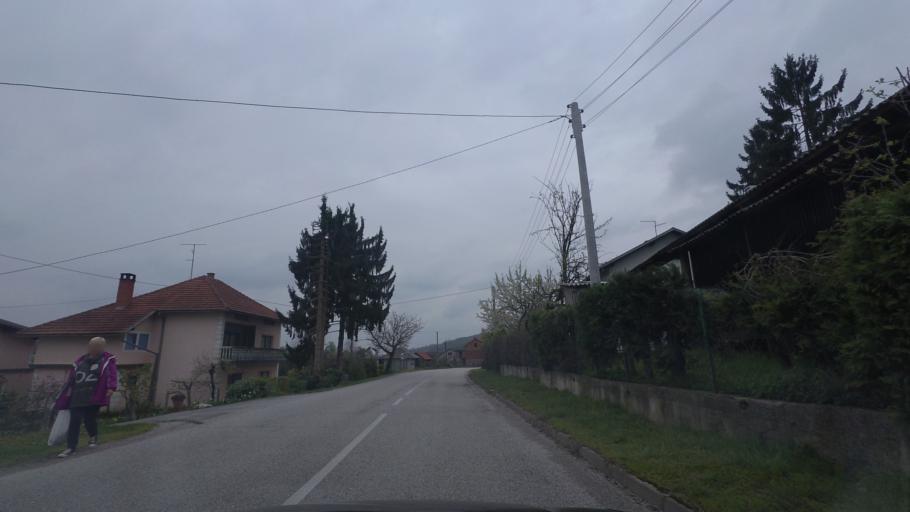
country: HR
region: Karlovacka
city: Ozalj
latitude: 45.6465
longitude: 15.5256
